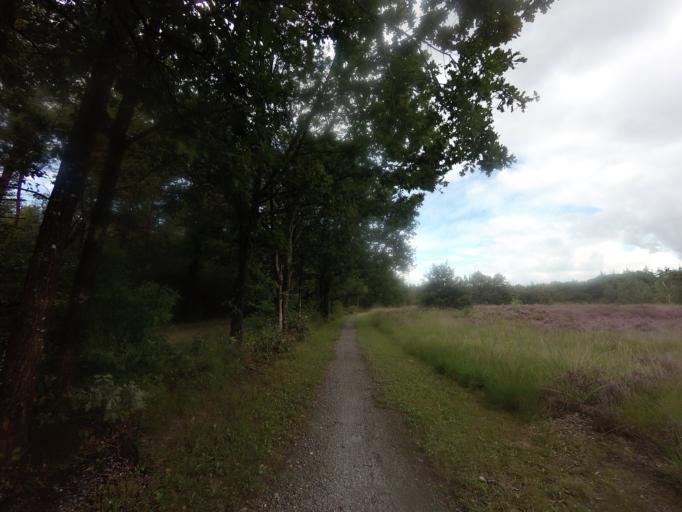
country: NL
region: Overijssel
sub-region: Gemeente Staphorst
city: Staphorst
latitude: 52.6438
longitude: 6.2664
